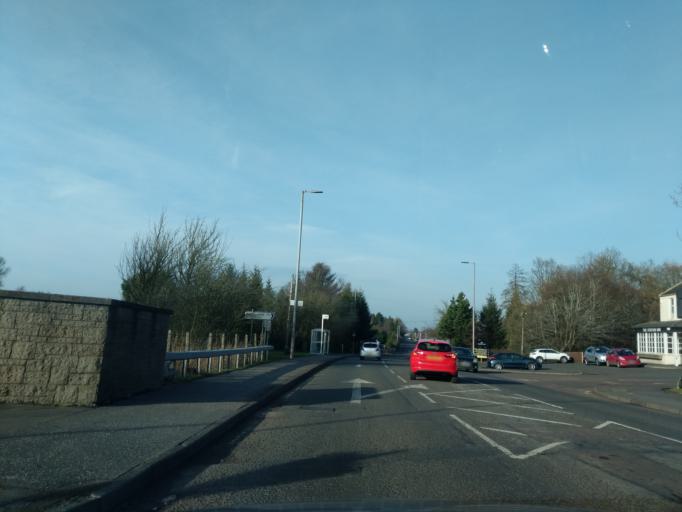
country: GB
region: Scotland
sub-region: South Lanarkshire
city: Carluke
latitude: 55.7148
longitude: -3.8322
